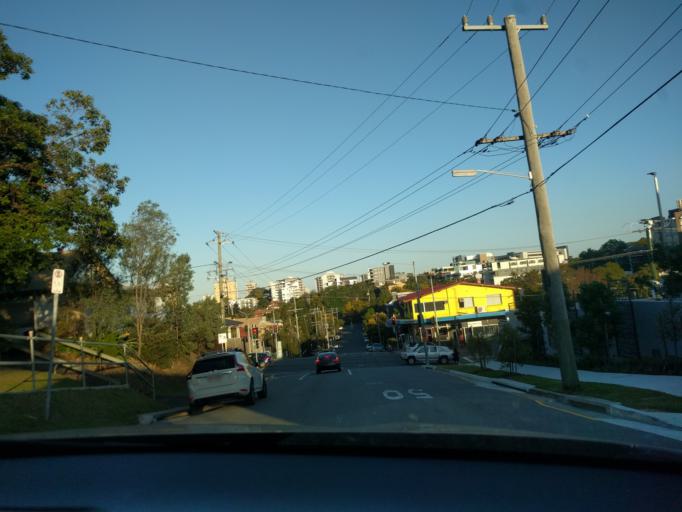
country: AU
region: Queensland
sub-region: Brisbane
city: Milton
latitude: -27.4733
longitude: 152.9954
